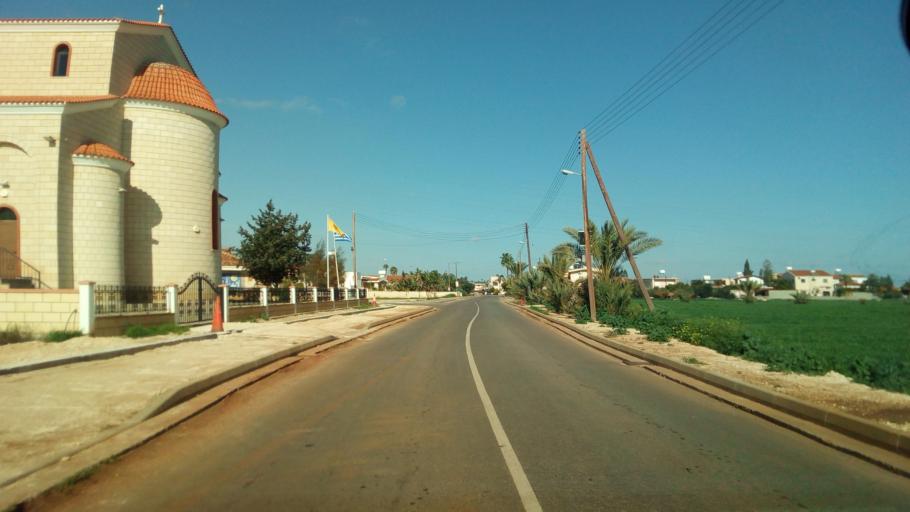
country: CY
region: Ammochostos
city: Avgorou
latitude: 35.0243
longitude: 33.8400
